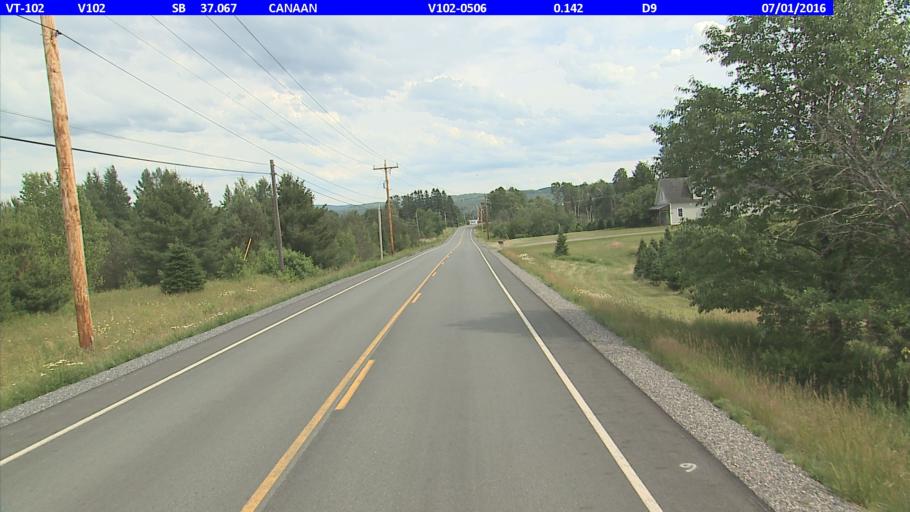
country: US
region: New Hampshire
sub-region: Coos County
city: Colebrook
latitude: 44.9126
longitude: -71.5084
